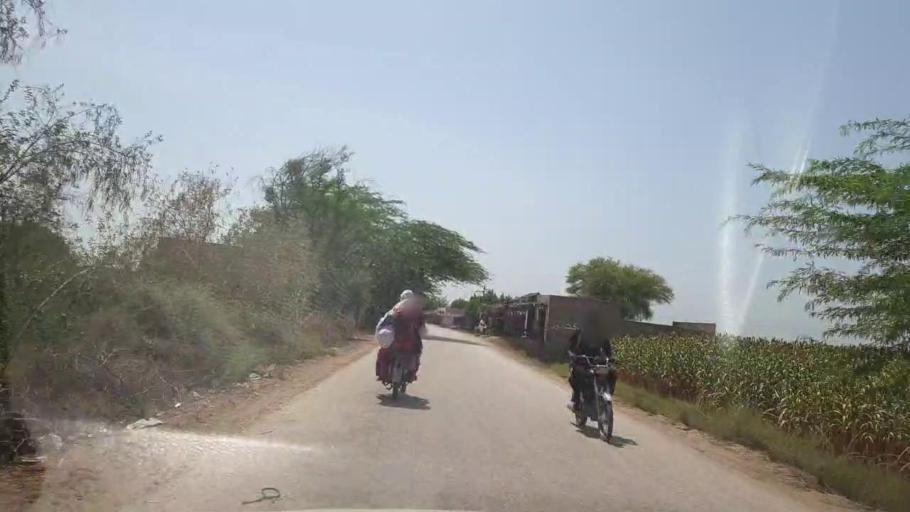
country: PK
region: Sindh
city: Bozdar
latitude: 27.0732
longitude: 68.5992
